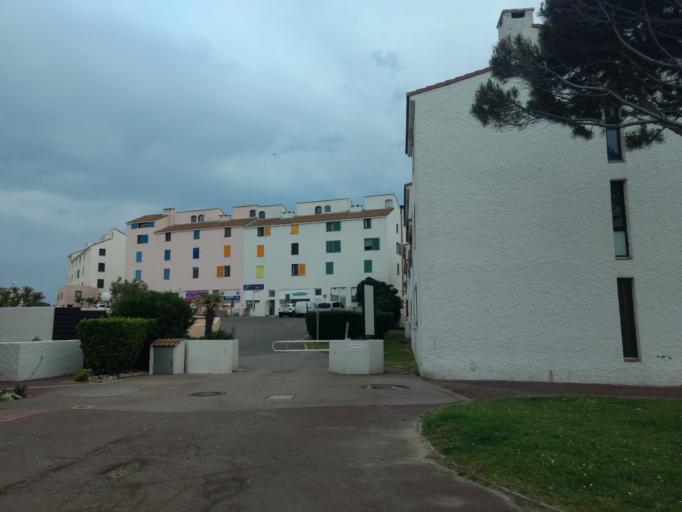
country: FR
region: Languedoc-Roussillon
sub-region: Departement des Pyrenees-Orientales
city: Le Barcares
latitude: 42.8154
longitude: 3.0197
